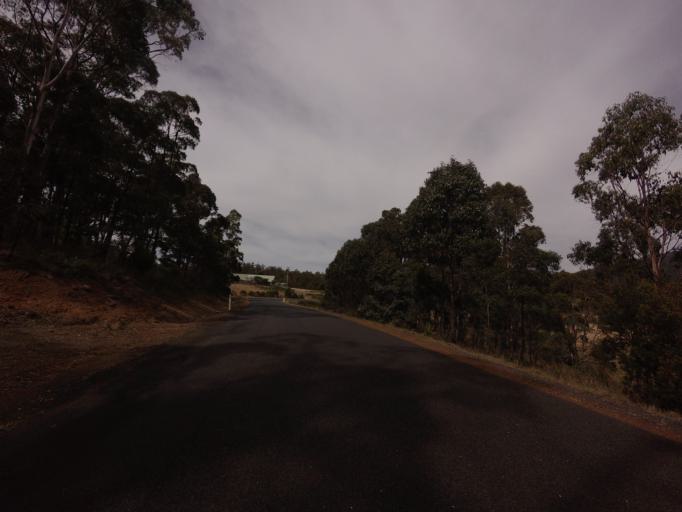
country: AU
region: Tasmania
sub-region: Sorell
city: Sorell
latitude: -42.5753
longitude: 147.5581
